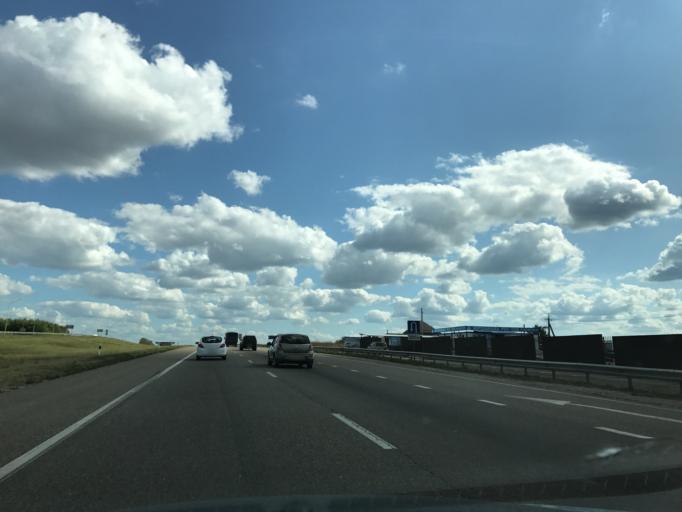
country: RU
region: Adygeya
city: Adygeysk
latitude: 44.9054
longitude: 39.1566
